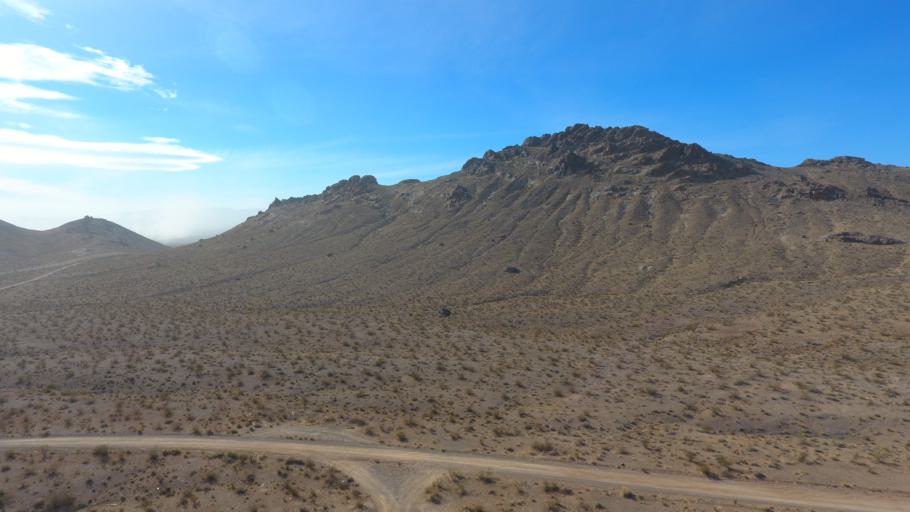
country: US
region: Nevada
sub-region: Nye County
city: Beatty
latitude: 36.9071
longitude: -116.7923
